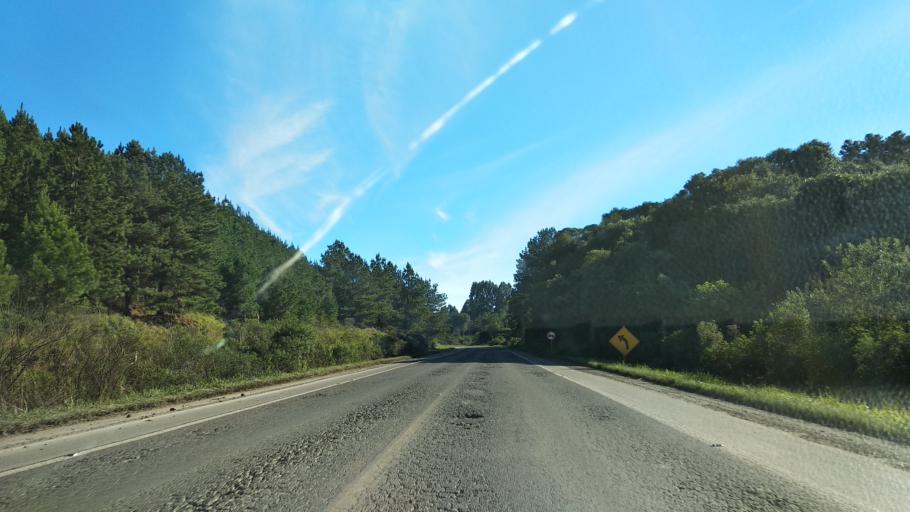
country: BR
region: Santa Catarina
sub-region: Campos Novos
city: Campos Novos
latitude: -27.3999
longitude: -51.1984
